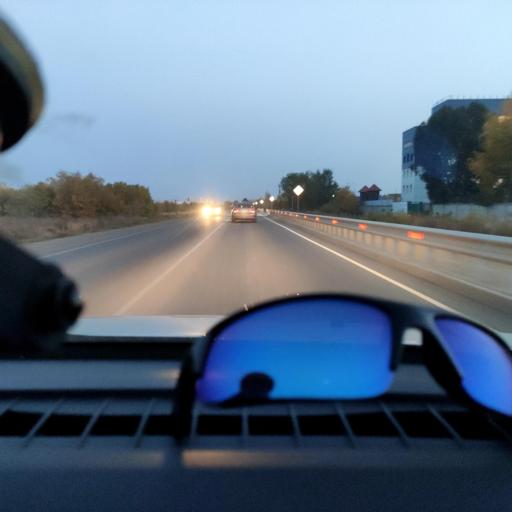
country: RU
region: Samara
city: Samara
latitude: 53.1262
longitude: 50.1129
